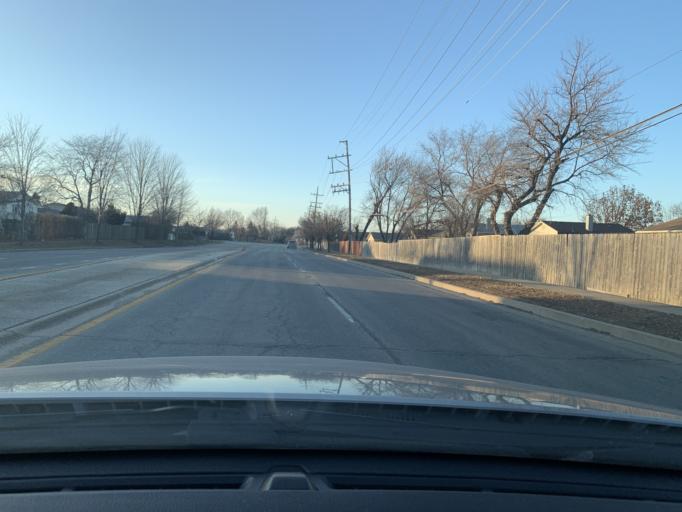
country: US
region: Illinois
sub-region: DuPage County
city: Itasca
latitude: 41.9971
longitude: -88.0337
